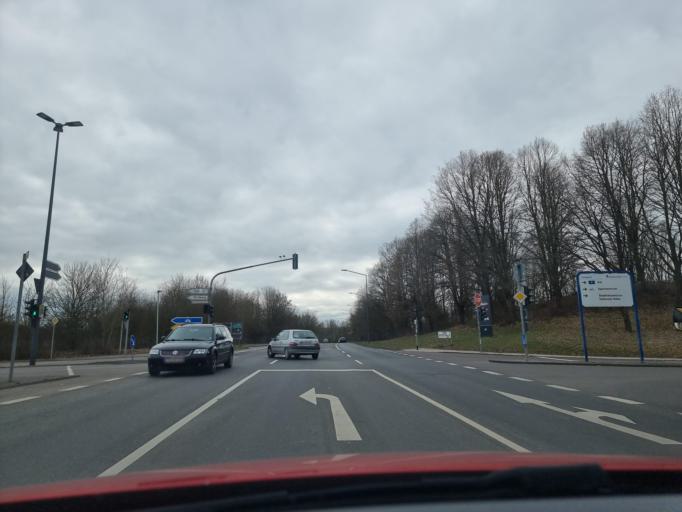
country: DE
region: Rheinland-Pfalz
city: Irsch
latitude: 49.7446
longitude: 6.6916
